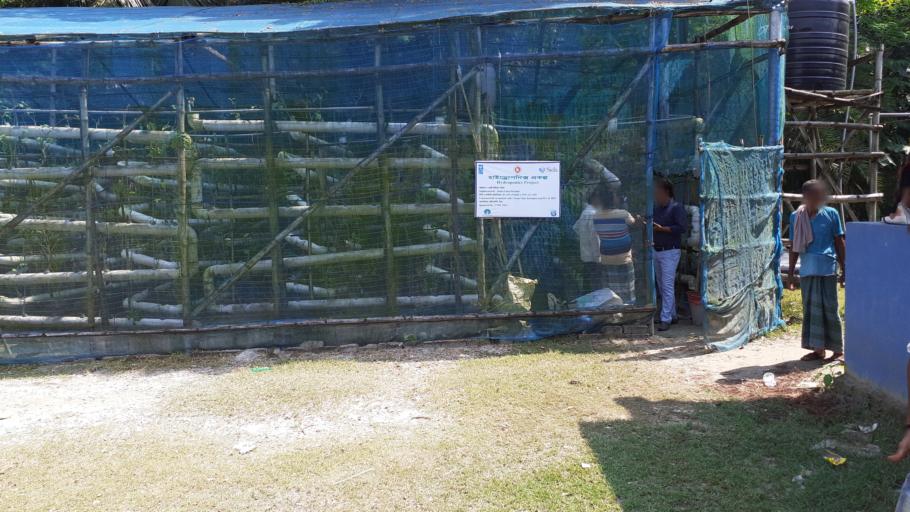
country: BD
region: Khulna
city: Phultala
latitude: 22.6414
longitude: 89.4217
